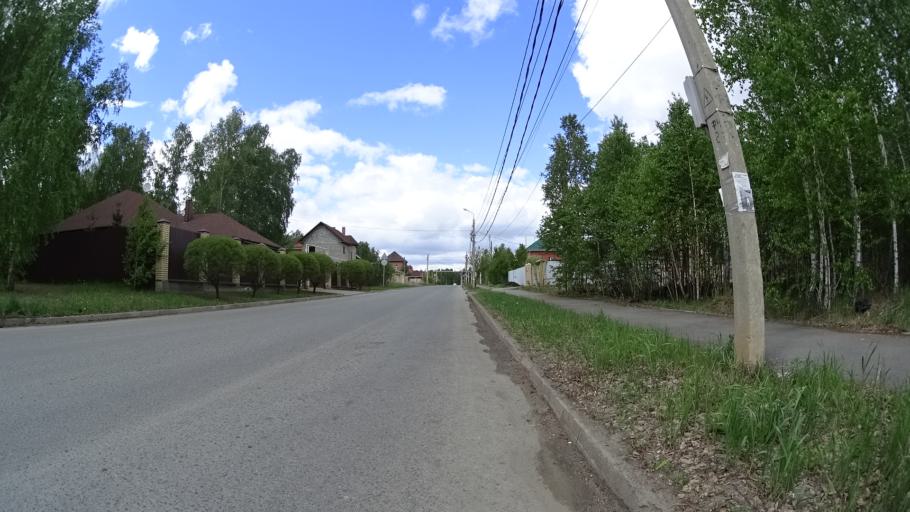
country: RU
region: Chelyabinsk
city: Sargazy
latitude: 55.1580
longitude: 61.2519
